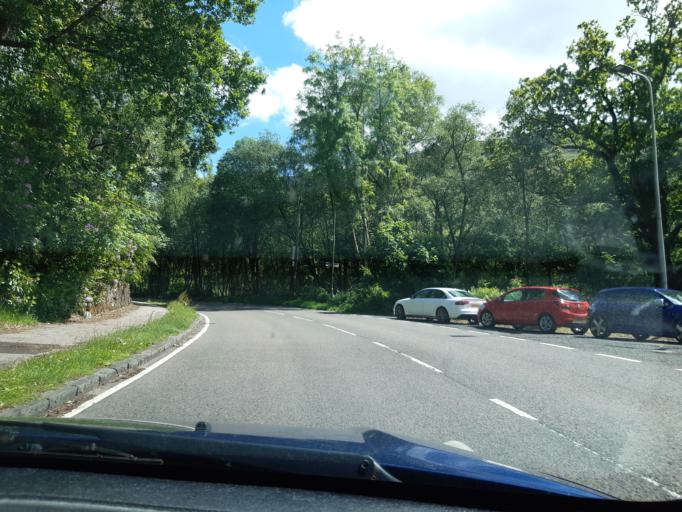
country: GB
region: Scotland
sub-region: Argyll and Bute
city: Garelochhead
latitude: 56.1980
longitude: -4.7443
